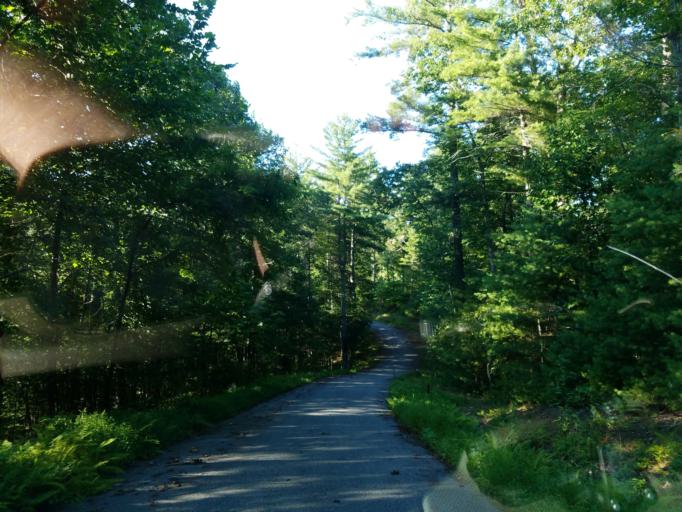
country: US
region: Georgia
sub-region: Union County
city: Blairsville
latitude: 34.7570
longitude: -84.1031
